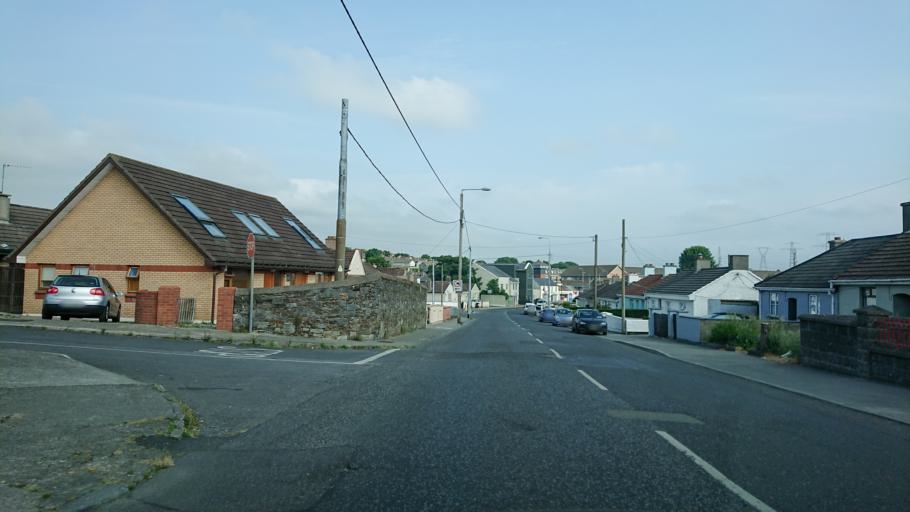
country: IE
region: Munster
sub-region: Waterford
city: Waterford
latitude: 52.2578
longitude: -7.1230
